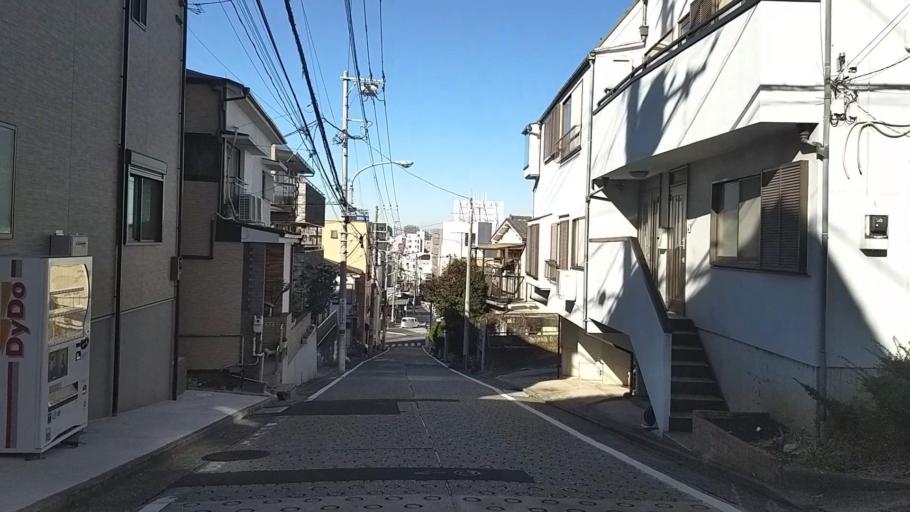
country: JP
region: Kanagawa
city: Yokohama
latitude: 35.4501
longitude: 139.6142
